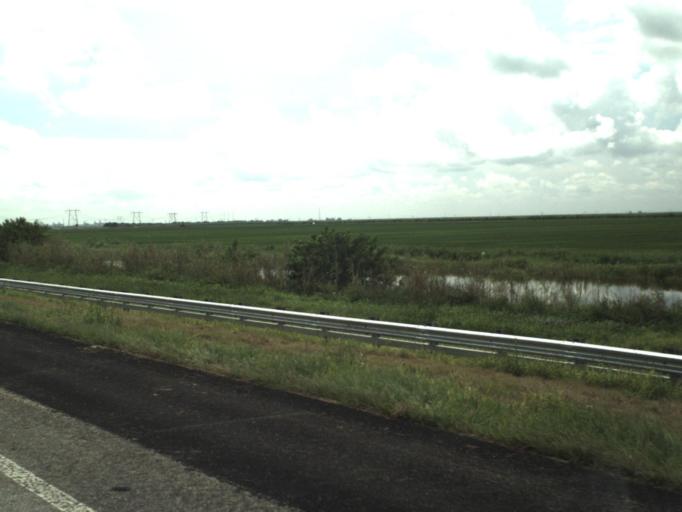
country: US
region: Florida
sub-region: Palm Beach County
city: Loxahatchee Groves
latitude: 26.7254
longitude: -80.4548
